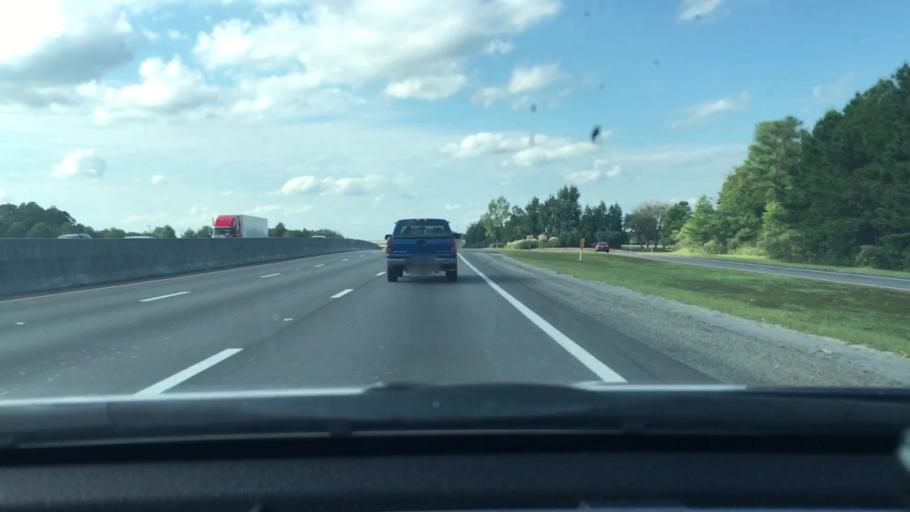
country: US
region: South Carolina
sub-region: Lexington County
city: Irmo
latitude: 34.0884
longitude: -81.1630
